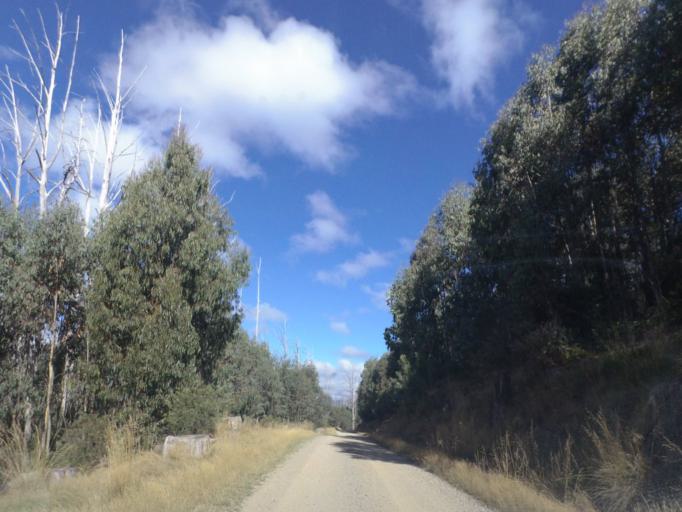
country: AU
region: Victoria
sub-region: Murrindindi
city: Alexandra
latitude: -37.4455
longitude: 145.8033
